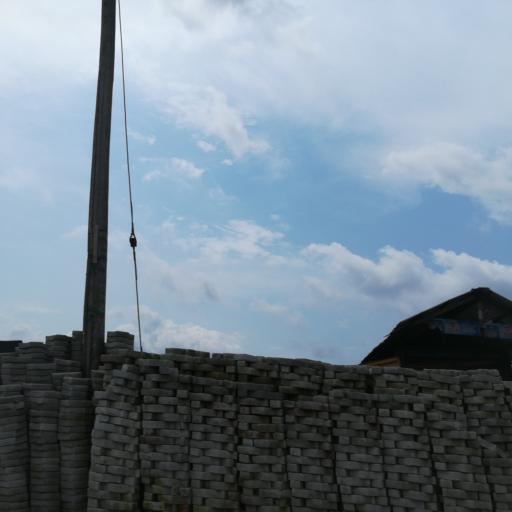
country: NG
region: Rivers
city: Port Harcourt
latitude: 4.8824
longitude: 7.0122
